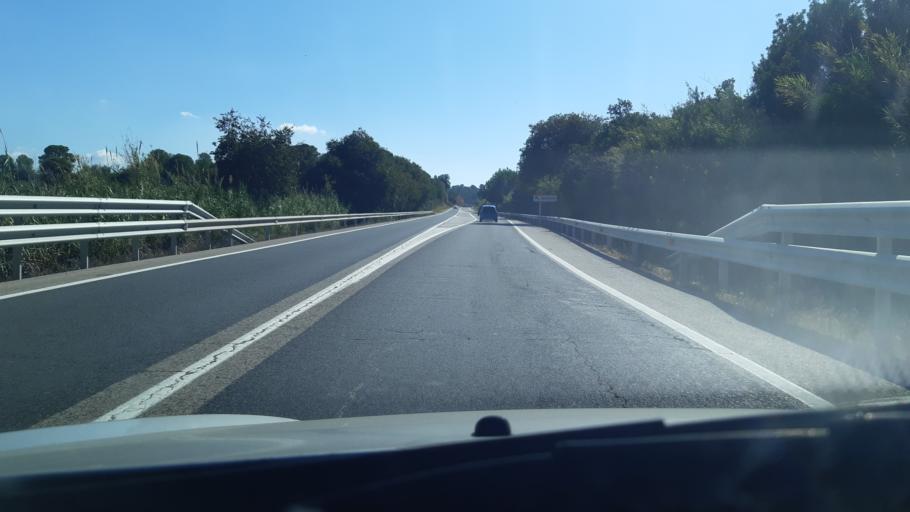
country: ES
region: Catalonia
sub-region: Provincia de Tarragona
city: Tivenys
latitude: 40.8912
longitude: 0.4901
